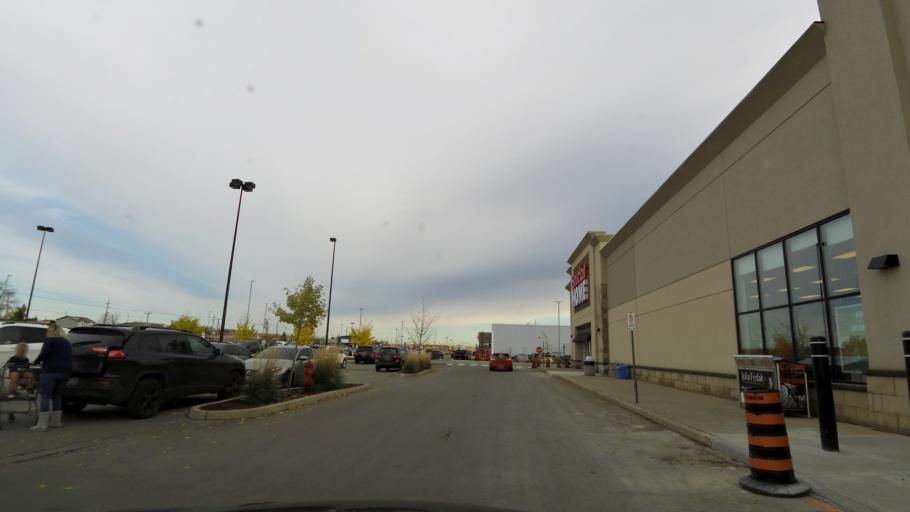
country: CA
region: Ontario
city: Hamilton
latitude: 43.1752
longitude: -79.7904
